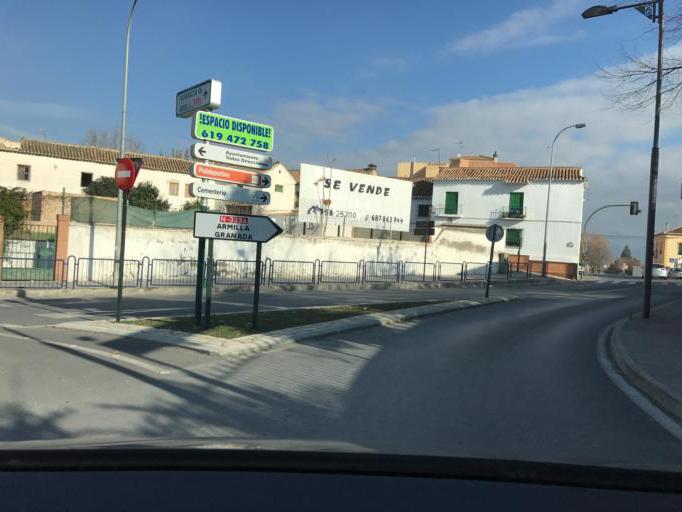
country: ES
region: Andalusia
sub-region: Provincia de Granada
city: Alhendin
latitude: 37.1061
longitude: -3.6428
